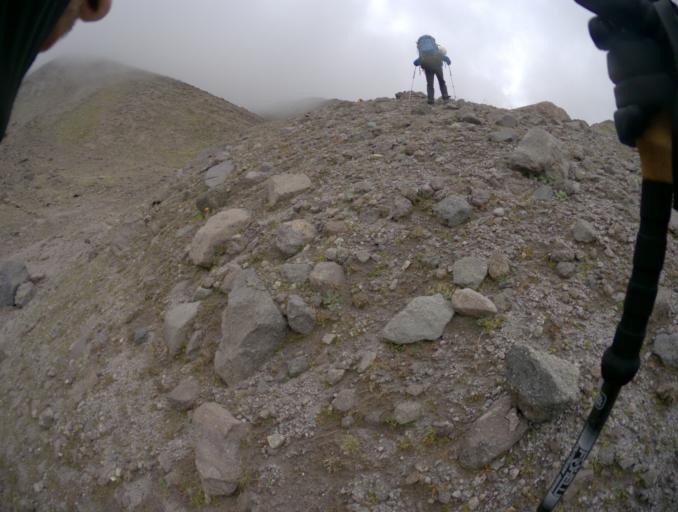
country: RU
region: Kabardino-Balkariya
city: Terskol
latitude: 43.3838
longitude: 42.3807
